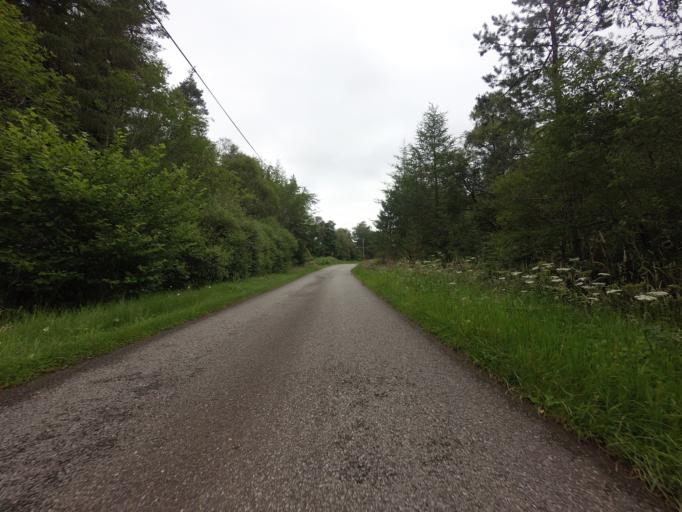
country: GB
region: Scotland
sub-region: Highland
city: Evanton
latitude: 57.9691
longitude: -4.4123
